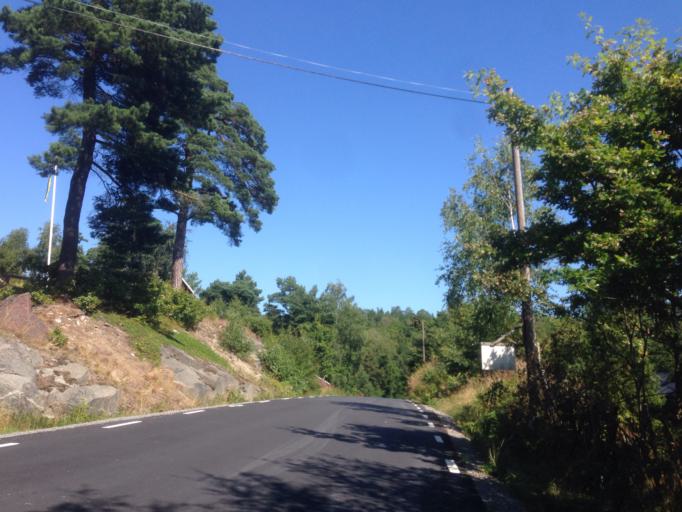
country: SE
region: Stockholm
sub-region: Vaxholms Kommun
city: Vaxholm
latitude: 59.3851
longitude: 18.3608
